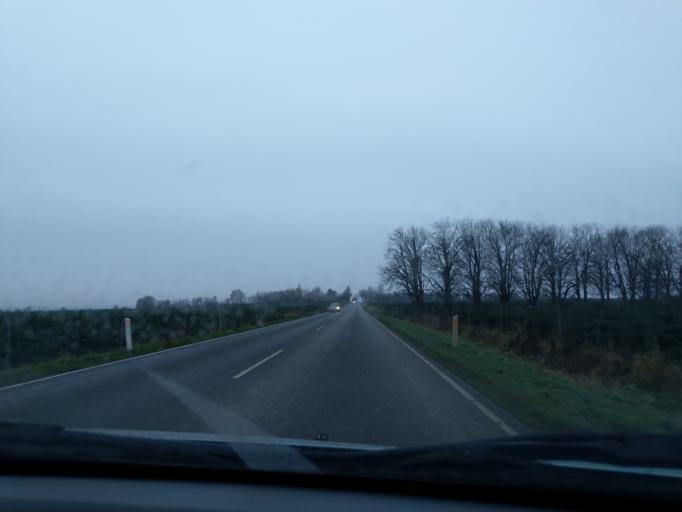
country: DK
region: Zealand
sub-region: Vordingborg Kommune
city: Orslev
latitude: 55.1196
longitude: 11.9781
